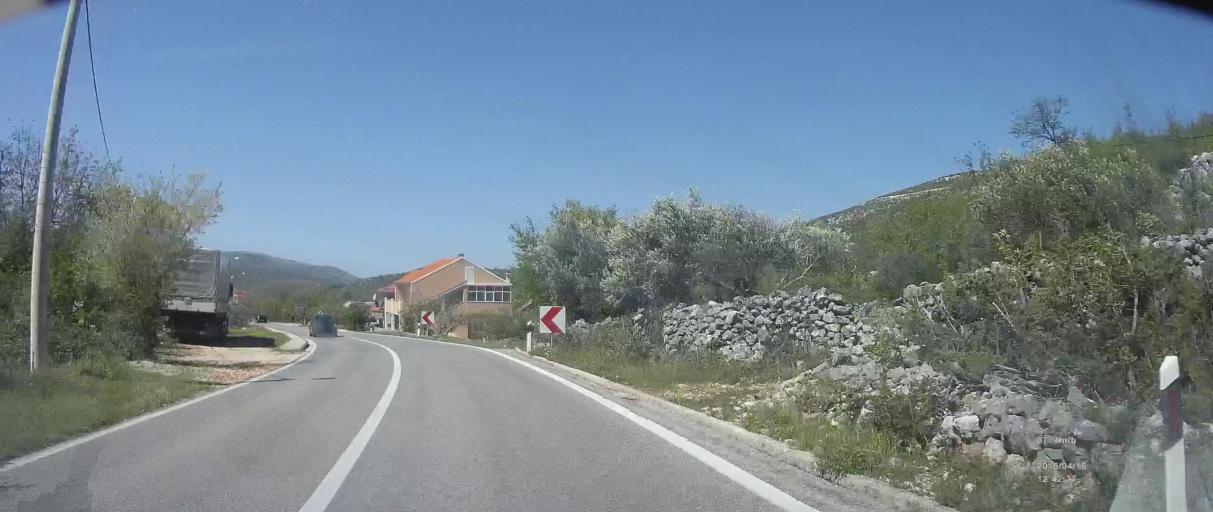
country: HR
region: Sibensko-Kniniska
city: Rogoznica
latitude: 43.6293
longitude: 16.0893
